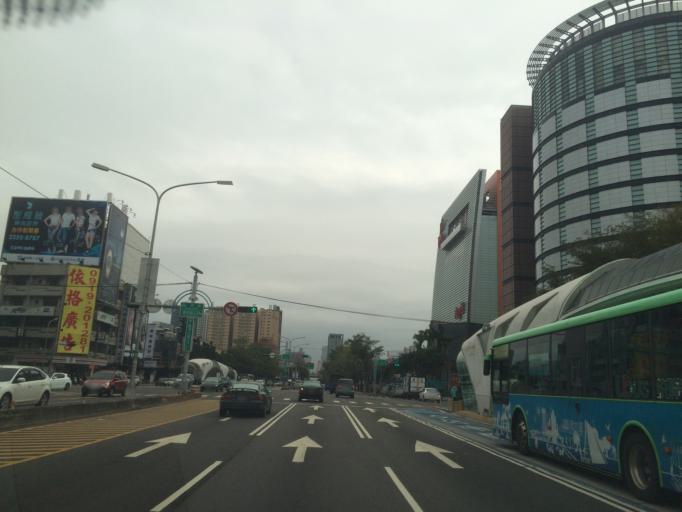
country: TW
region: Taiwan
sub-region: Taichung City
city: Taichung
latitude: 24.1663
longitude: 120.6430
